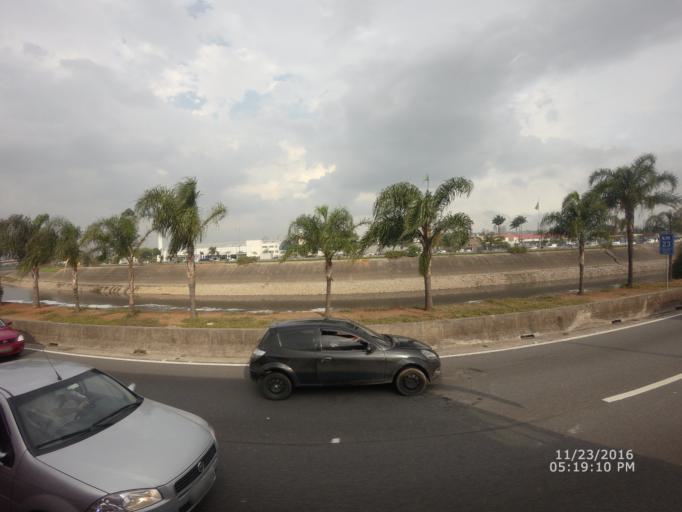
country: BR
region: Sao Paulo
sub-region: Guarulhos
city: Guarulhos
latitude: -23.5111
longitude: -46.5565
